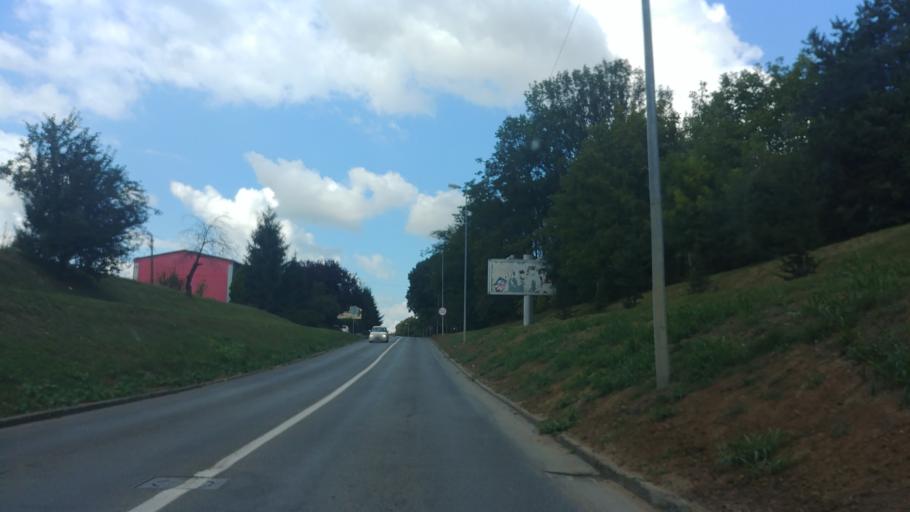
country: BA
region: Brcko
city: Brcko
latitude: 44.8653
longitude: 18.8207
